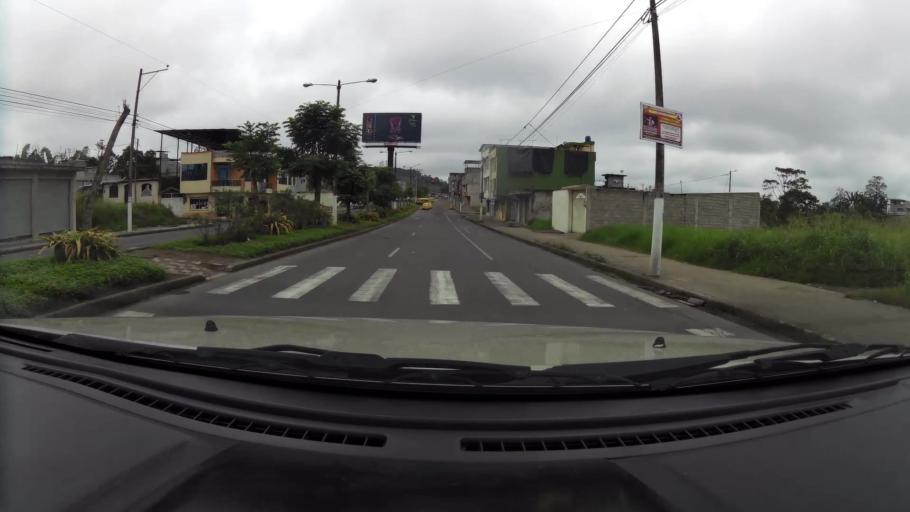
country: EC
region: Santo Domingo de los Tsachilas
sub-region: Canton Santo Domingo de los Colorados
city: Santo Domingo de los Colorados
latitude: -0.2394
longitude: -79.1807
